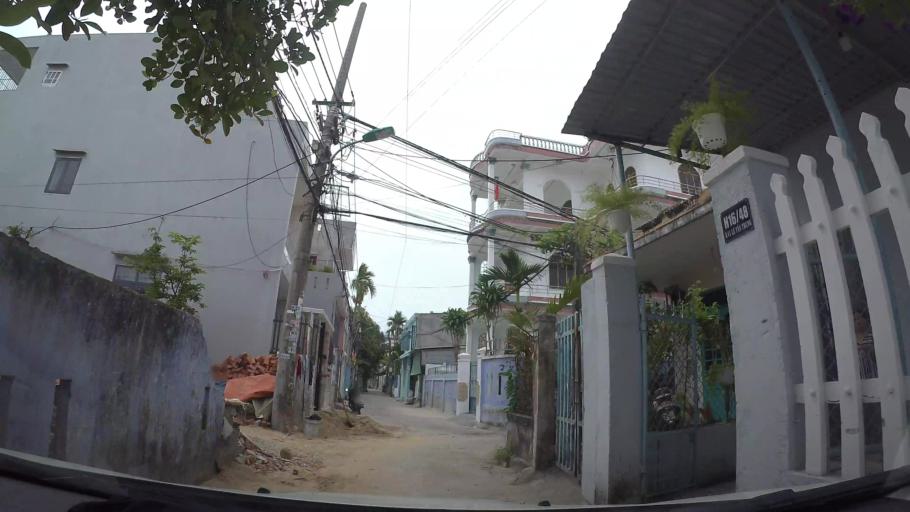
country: VN
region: Da Nang
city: Son Tra
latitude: 16.0975
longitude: 108.2486
